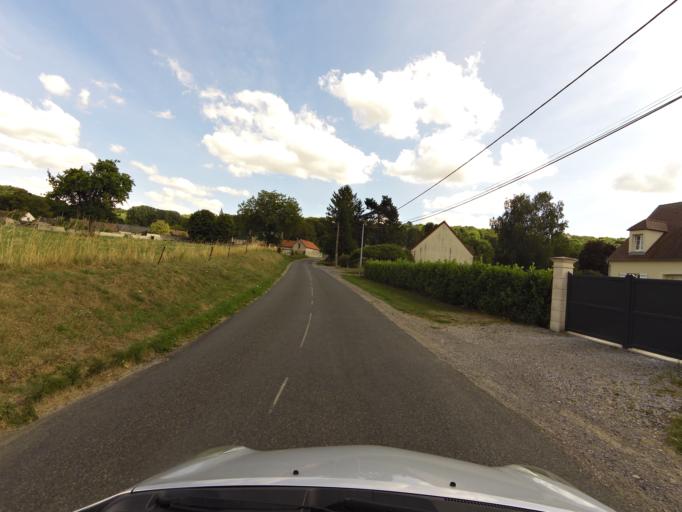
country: FR
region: Picardie
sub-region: Departement de l'Aisne
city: Bruyeres-et-Montberault
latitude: 49.5086
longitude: 3.6232
